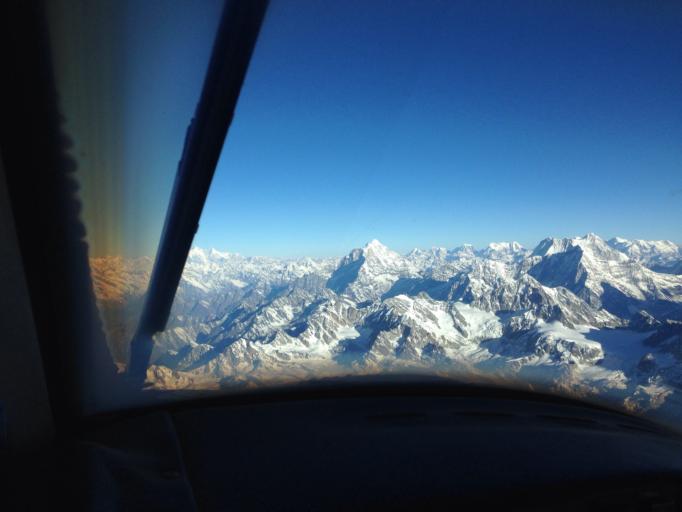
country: NP
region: Eastern Region
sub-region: Sagarmatha Zone
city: Namche Bazar
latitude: 27.7221
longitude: 86.4857
